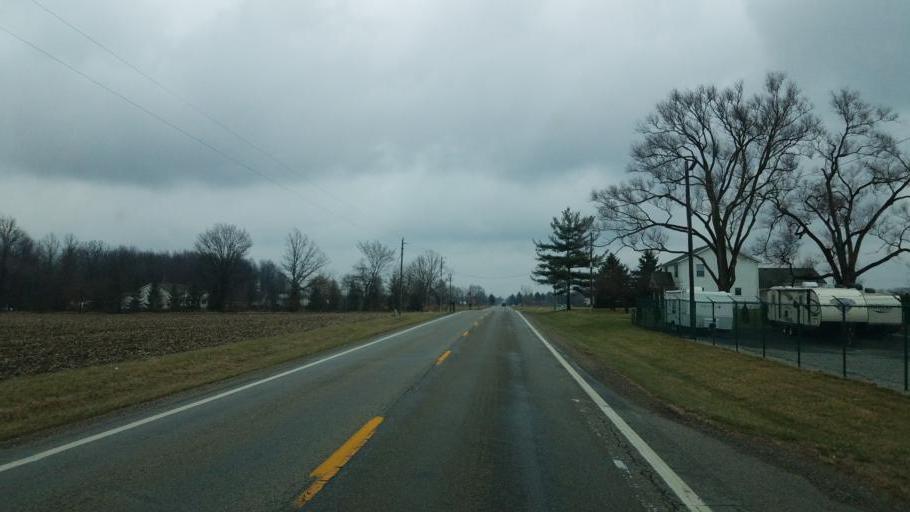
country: US
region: Ohio
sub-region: Delaware County
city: Ashley
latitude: 40.4077
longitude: -82.9222
